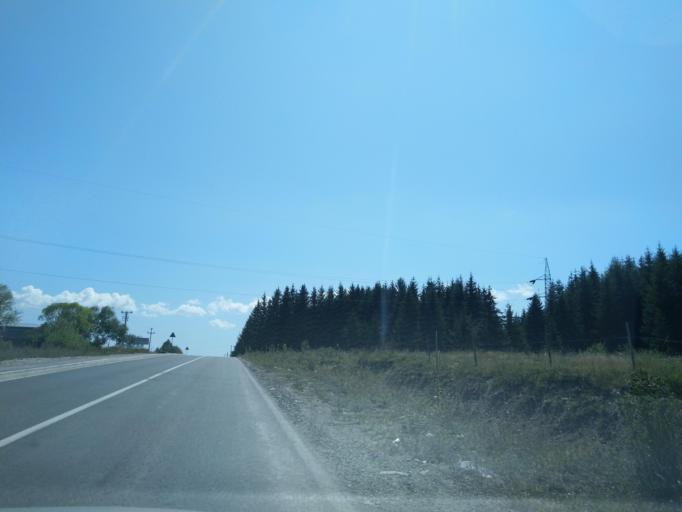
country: RS
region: Central Serbia
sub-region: Zlatiborski Okrug
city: Sjenica
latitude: 43.2808
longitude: 19.9732
